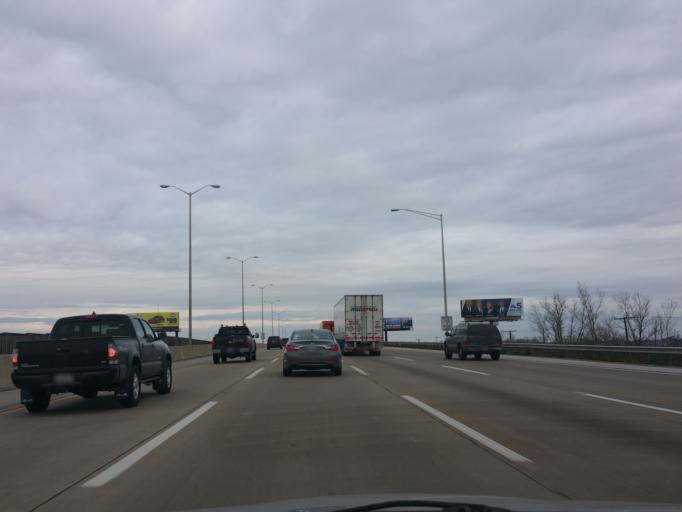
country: US
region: Illinois
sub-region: Cook County
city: Palos Hills
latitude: 41.7129
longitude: -87.8008
